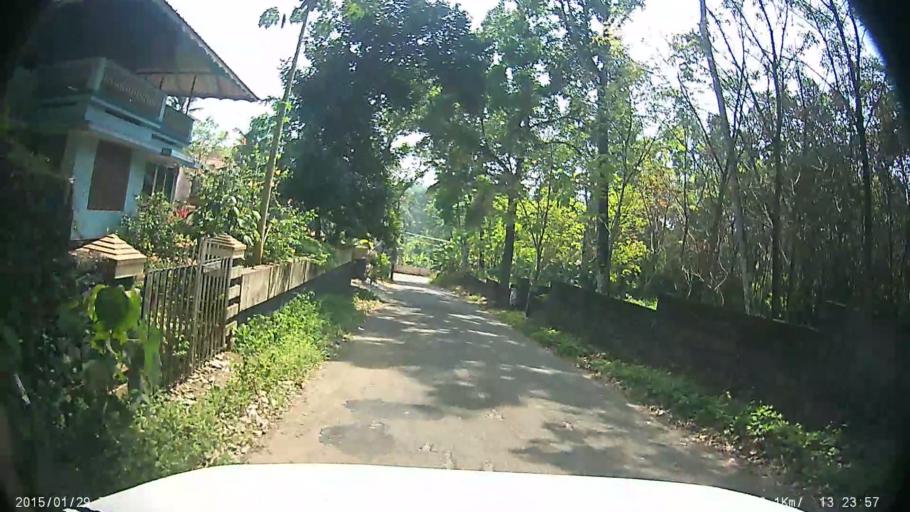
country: IN
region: Kerala
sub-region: Kottayam
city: Palackattumala
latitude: 9.7577
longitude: 76.5570
